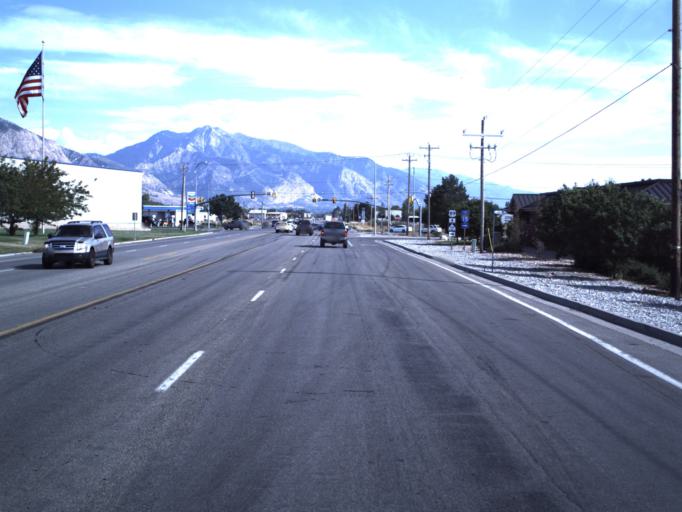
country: US
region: Utah
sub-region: Weber County
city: Pleasant View
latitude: 41.3081
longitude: -112.0069
